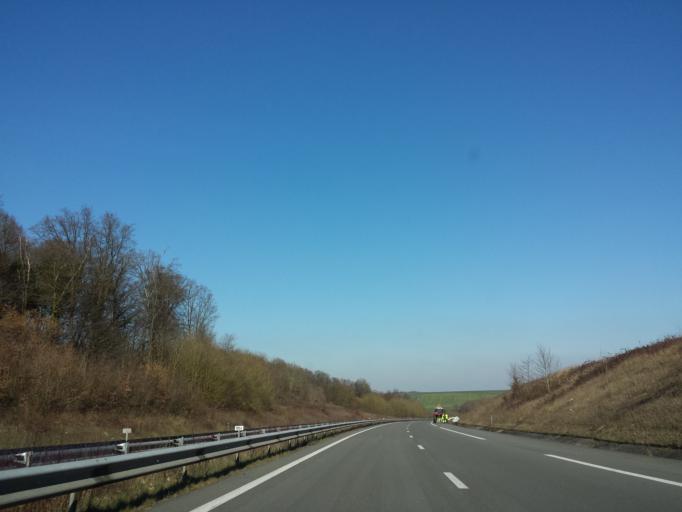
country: FR
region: Picardie
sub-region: Departement de l'Oise
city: Breteuil
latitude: 49.6663
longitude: 2.2085
